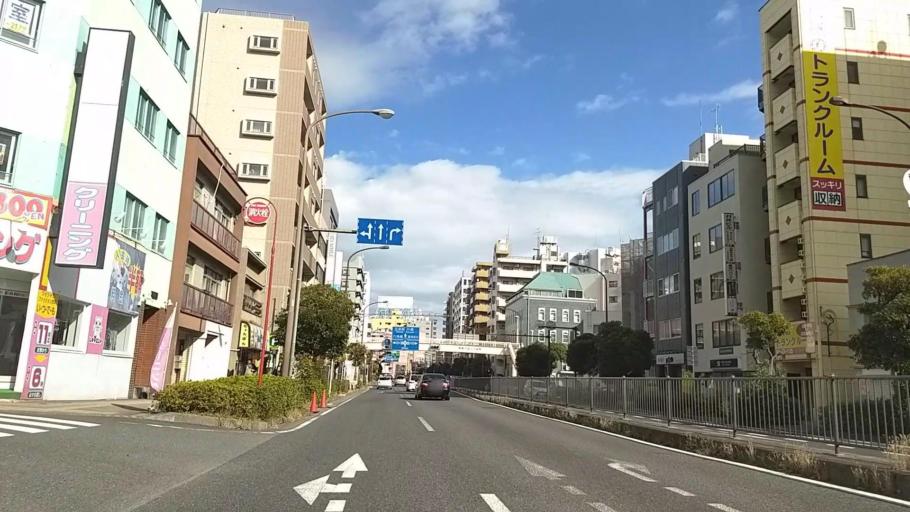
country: JP
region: Kanagawa
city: Yokohama
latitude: 35.4782
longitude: 139.6296
